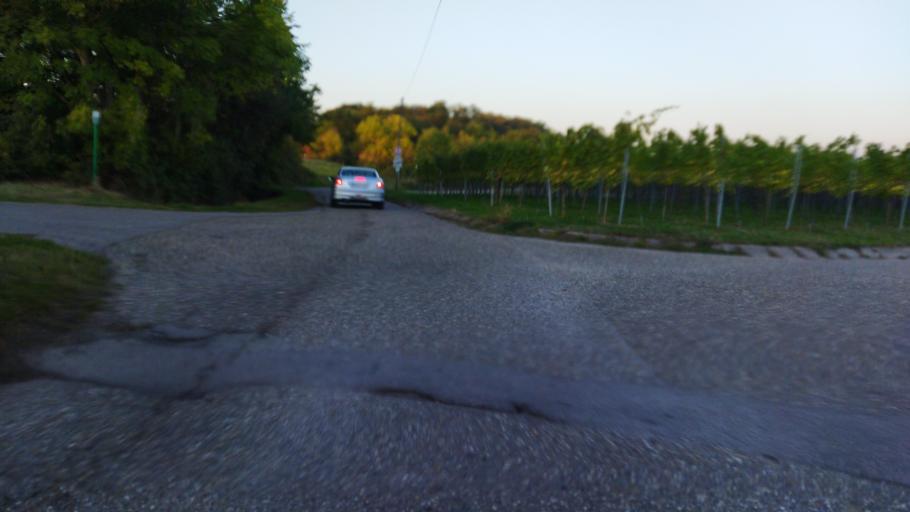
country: DE
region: Baden-Wuerttemberg
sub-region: Regierungsbezirk Stuttgart
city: Cleebronn
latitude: 49.0449
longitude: 9.0564
